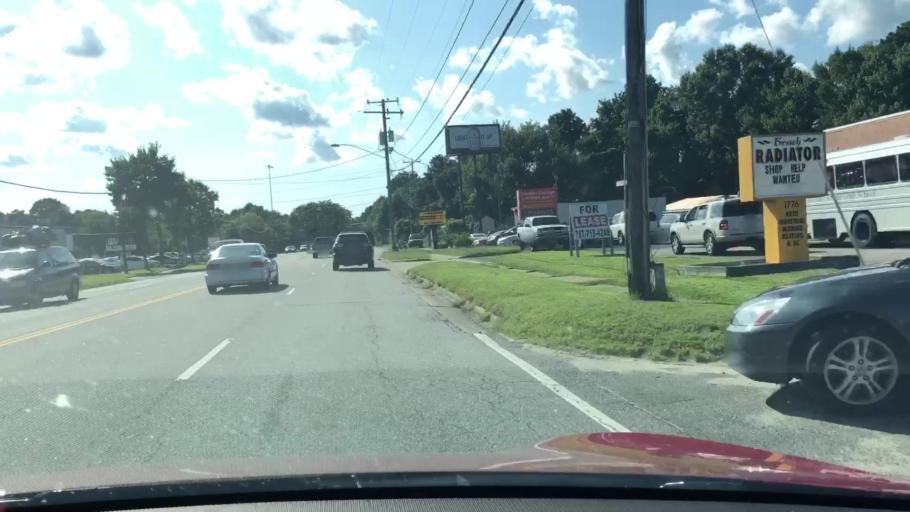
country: US
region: Virginia
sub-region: City of Virginia Beach
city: Virginia Beach
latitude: 36.8432
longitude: -76.0260
